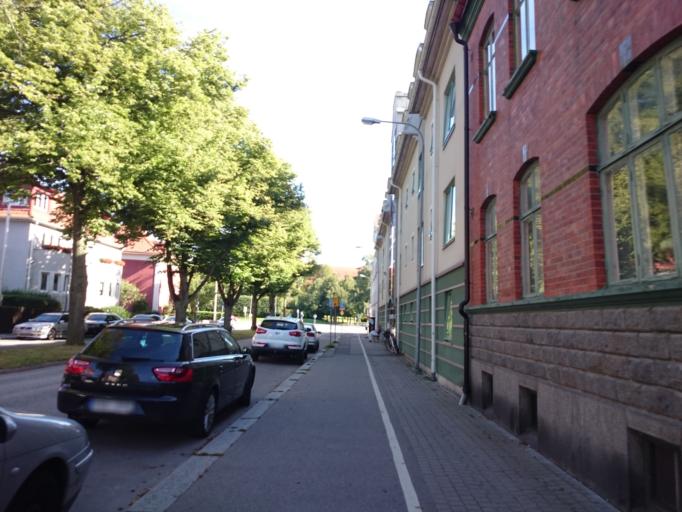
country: SE
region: Blekinge
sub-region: Karlshamns Kommun
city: Karlshamn
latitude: 56.1674
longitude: 14.8709
